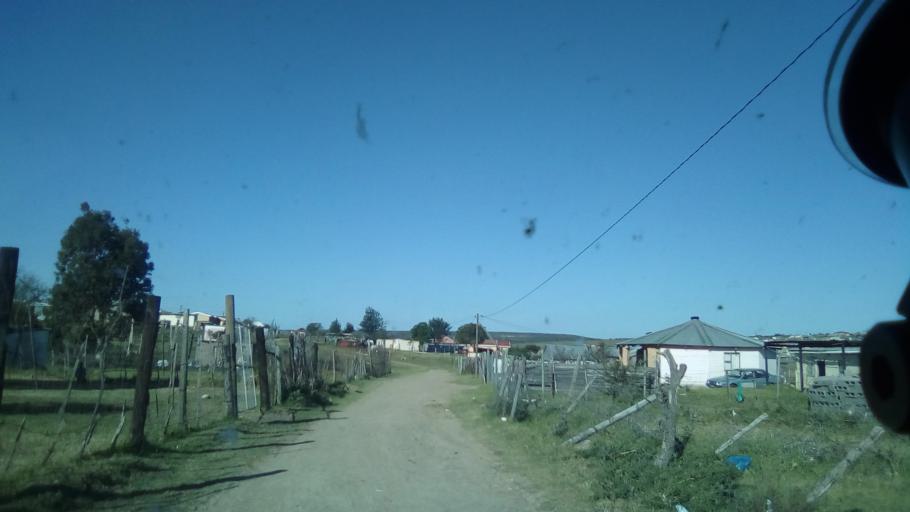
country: ZA
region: Eastern Cape
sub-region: Buffalo City Metropolitan Municipality
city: Bhisho
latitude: -32.8265
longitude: 27.3676
